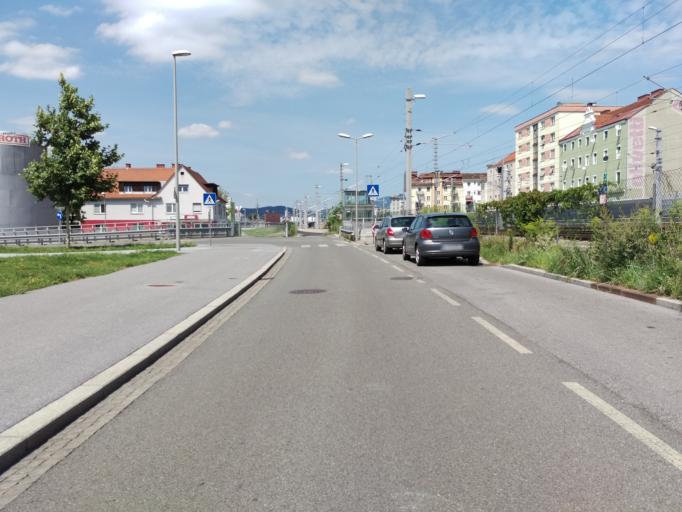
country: AT
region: Styria
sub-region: Graz Stadt
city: Wetzelsdorf
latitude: 47.0674
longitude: 15.4185
